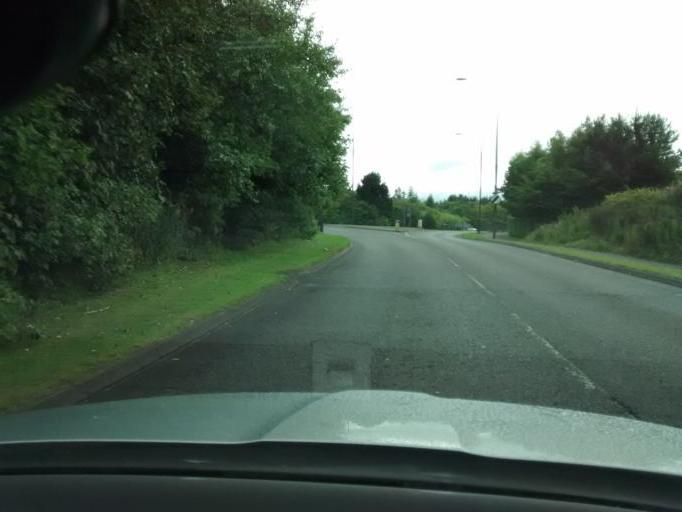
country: GB
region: Scotland
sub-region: West Lothian
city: West Calder
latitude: 55.8911
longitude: -3.5700
